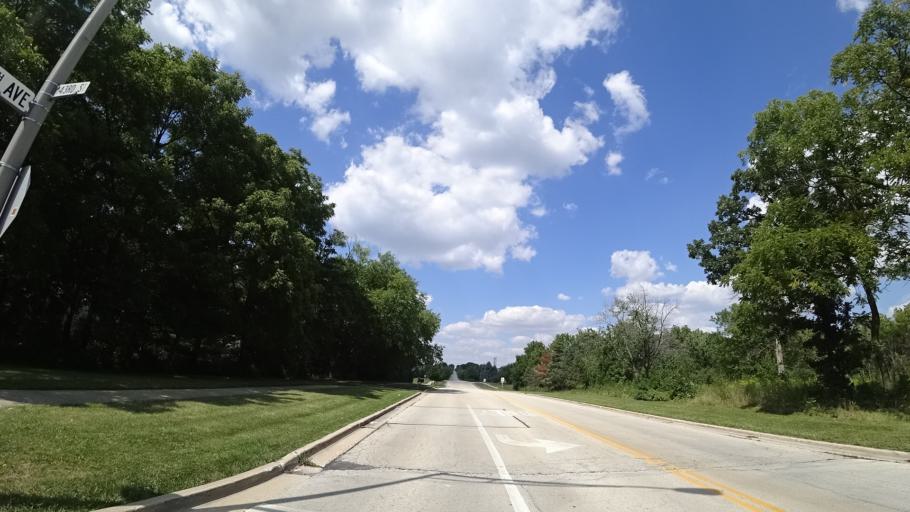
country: US
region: Illinois
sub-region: Cook County
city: Palos Park
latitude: 41.6313
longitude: -87.8148
